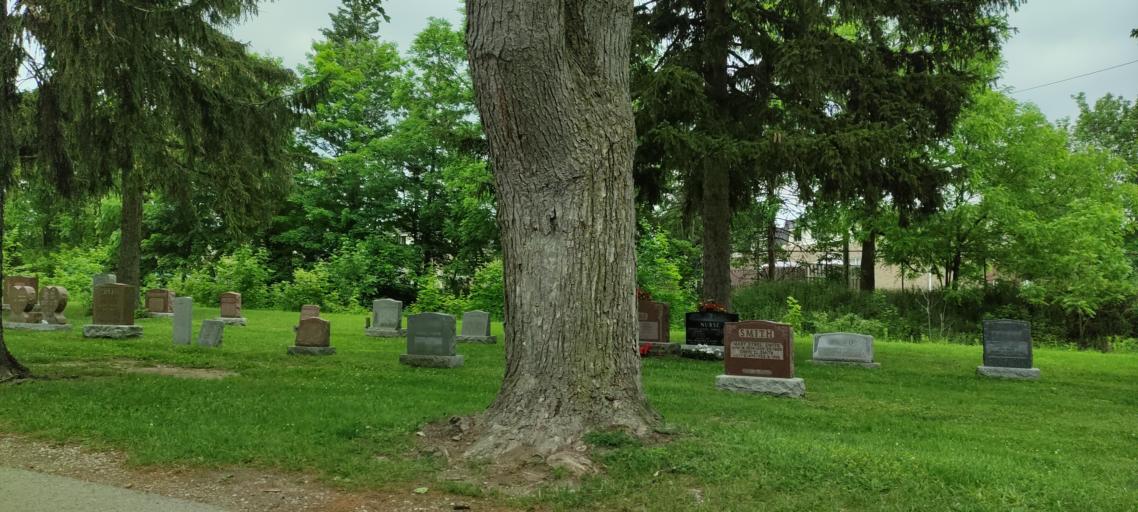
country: CA
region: Ontario
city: Stratford
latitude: 43.3737
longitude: -81.0005
